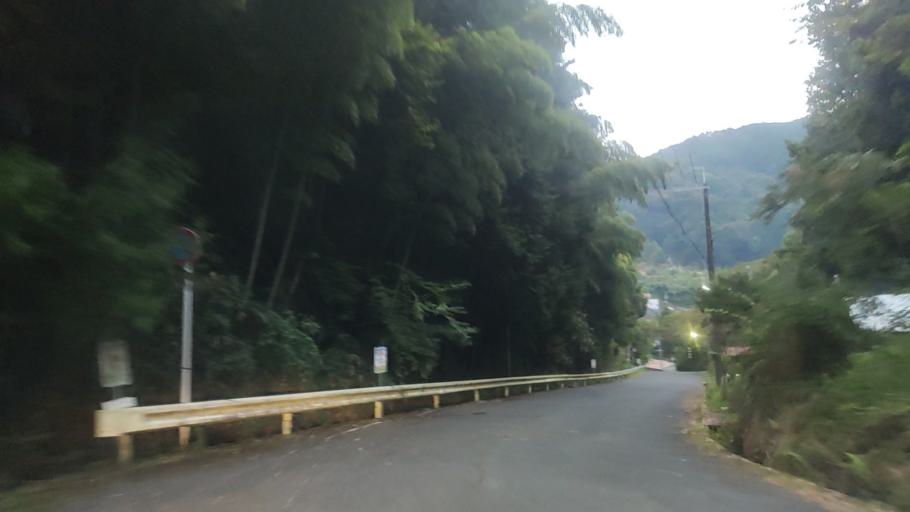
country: JP
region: Wakayama
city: Hashimoto
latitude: 34.3689
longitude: 135.6019
